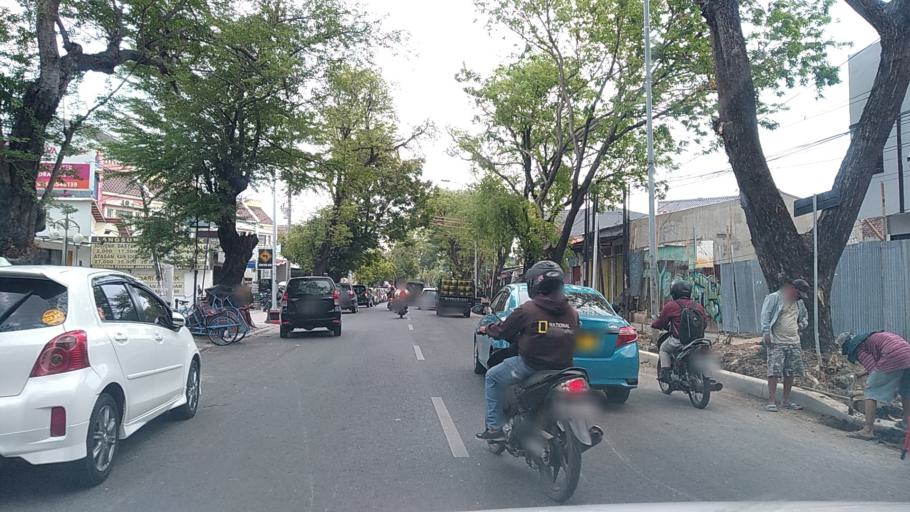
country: ID
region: Central Java
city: Semarang
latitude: -6.9803
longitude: 110.4033
